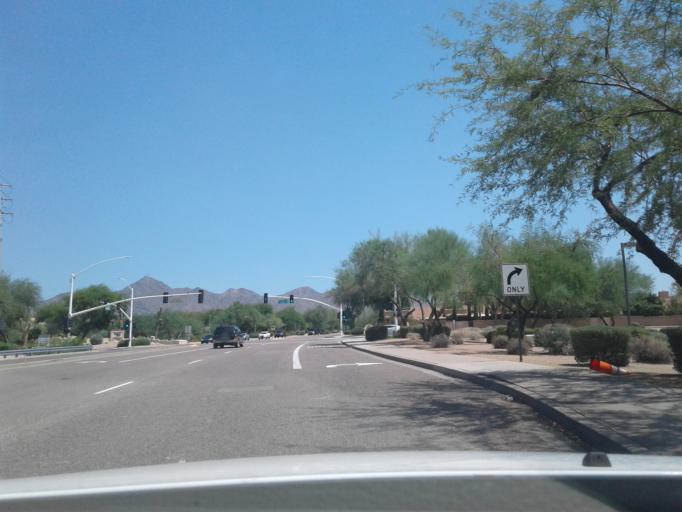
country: US
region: Arizona
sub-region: Maricopa County
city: Paradise Valley
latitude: 33.6186
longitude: -111.8878
